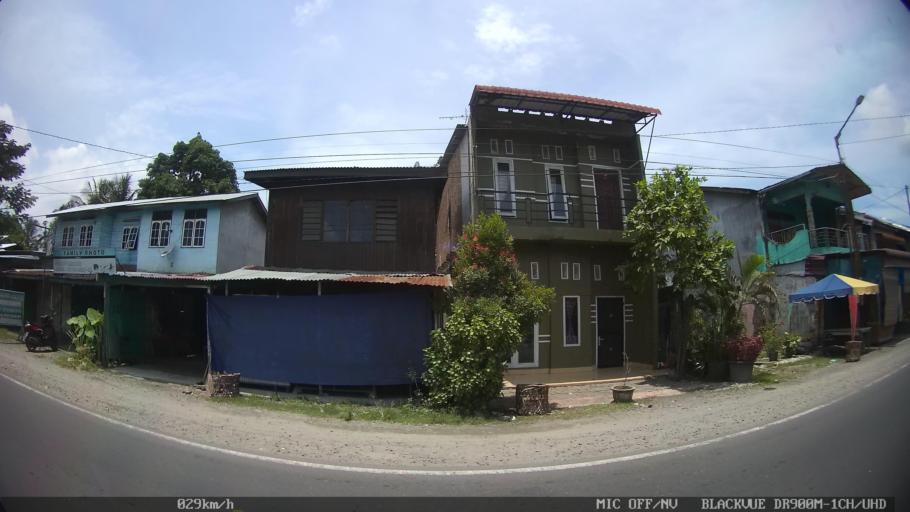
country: ID
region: North Sumatra
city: Labuhan Deli
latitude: 3.7434
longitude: 98.6747
